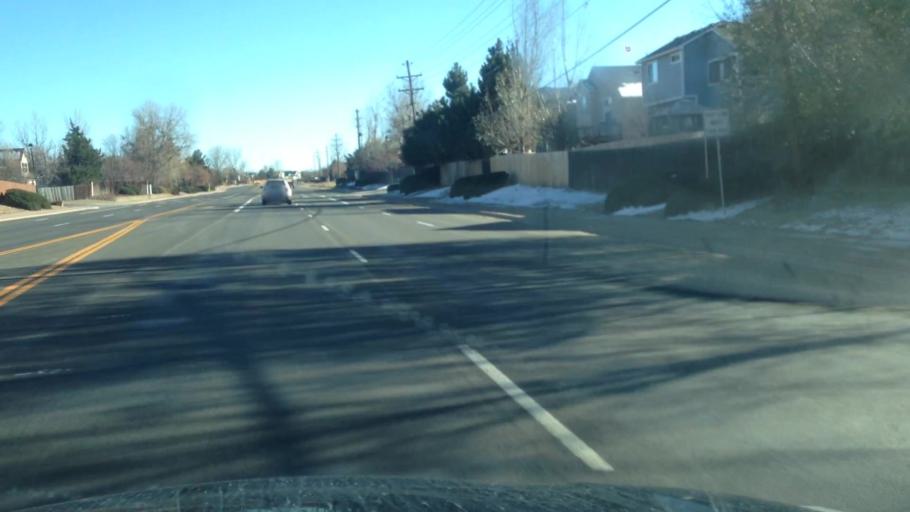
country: US
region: Colorado
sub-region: Douglas County
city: Stonegate
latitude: 39.5628
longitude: -104.7989
